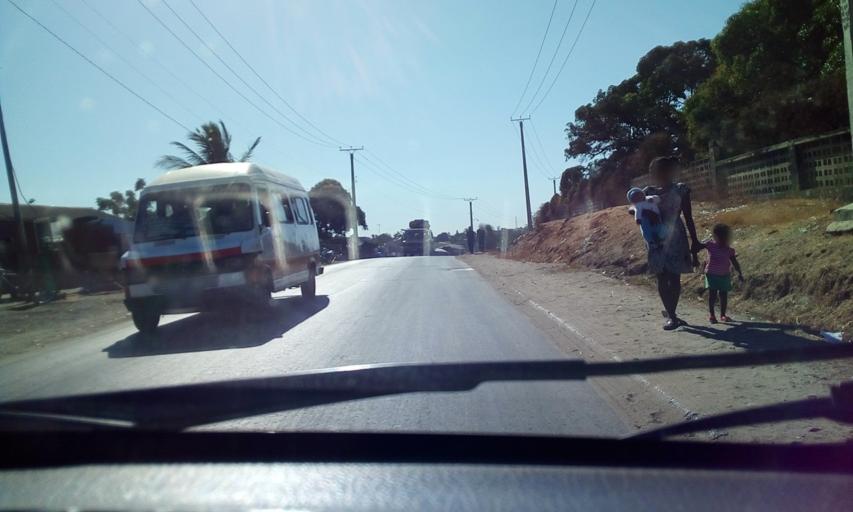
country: MG
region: Boeny
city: Mahajanga
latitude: -15.7186
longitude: 46.3295
